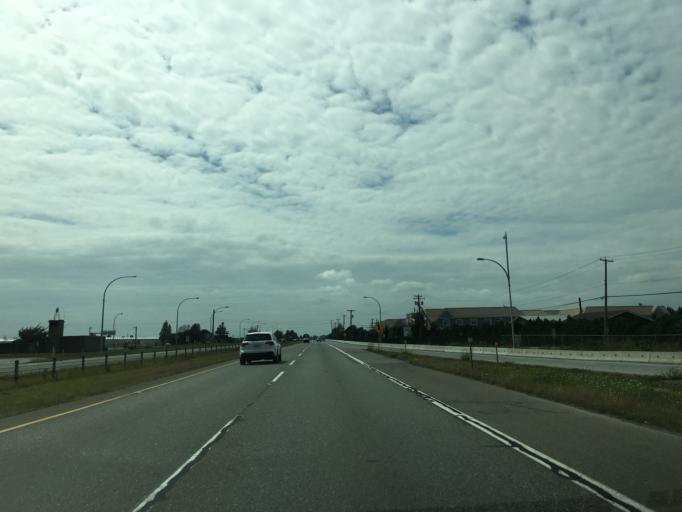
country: CA
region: British Columbia
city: Delta
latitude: 49.0906
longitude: -122.9610
